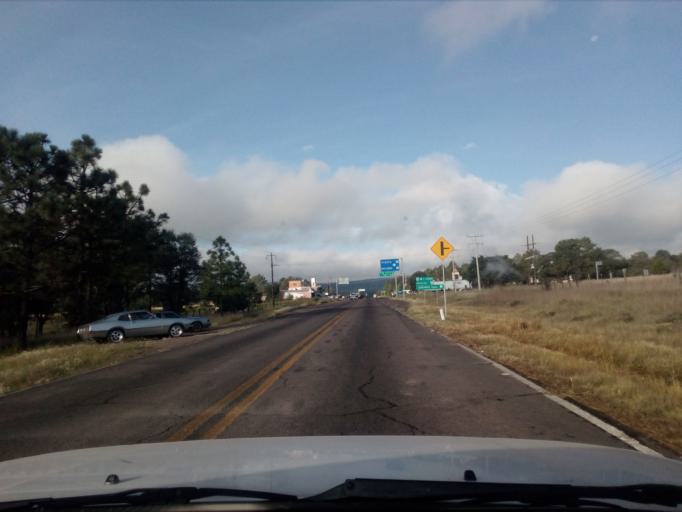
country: MX
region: Durango
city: Victoria de Durango
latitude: 23.9255
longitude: -104.9385
